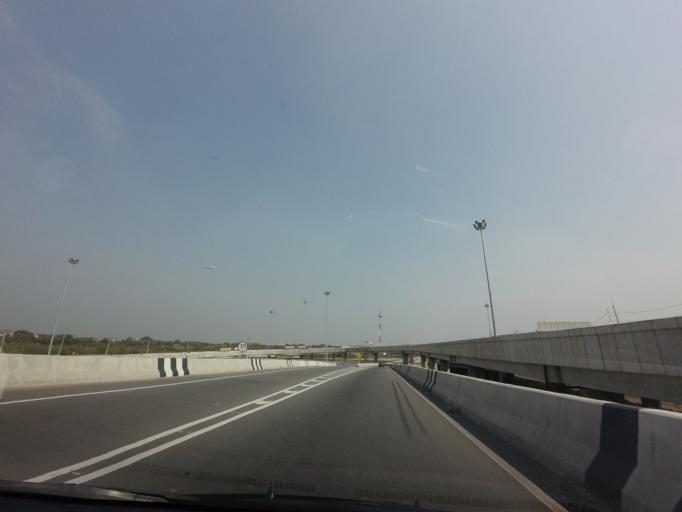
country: TH
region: Bangkok
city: Lat Krabang
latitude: 13.7564
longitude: 100.7469
